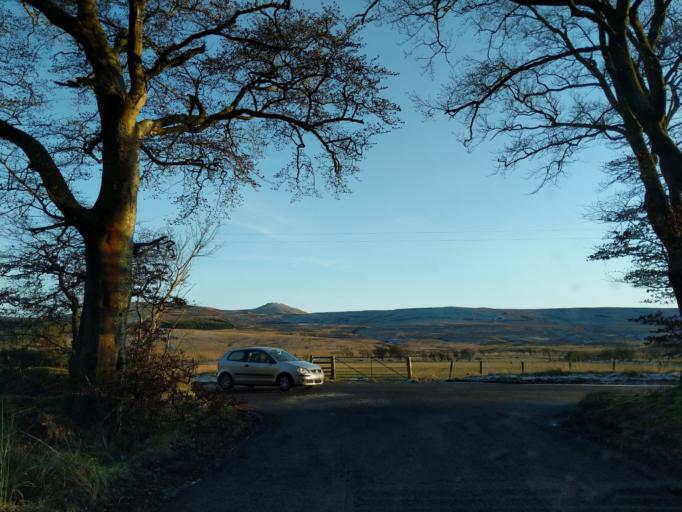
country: GB
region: Scotland
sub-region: Edinburgh
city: Balerno
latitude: 55.8551
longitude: -3.3602
